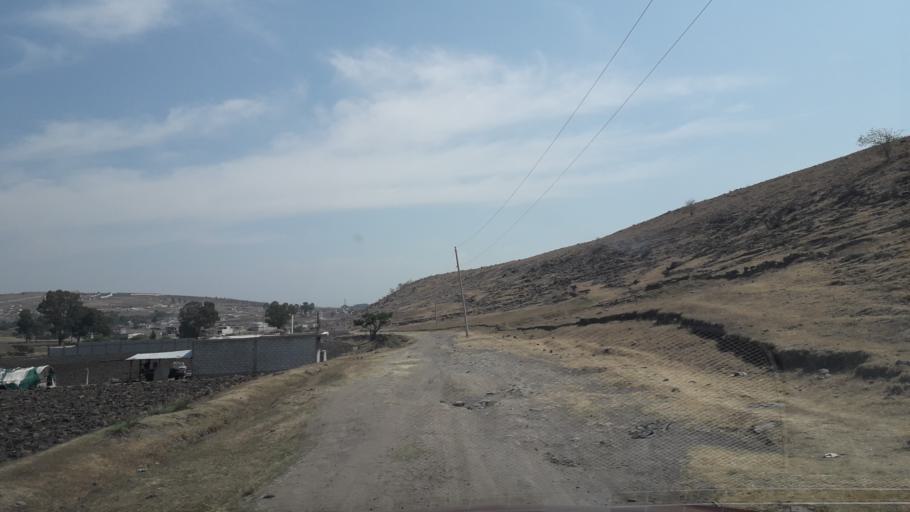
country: MX
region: Puebla
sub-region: Puebla
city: San Andres Azumiatla
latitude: 18.9217
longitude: -98.2569
